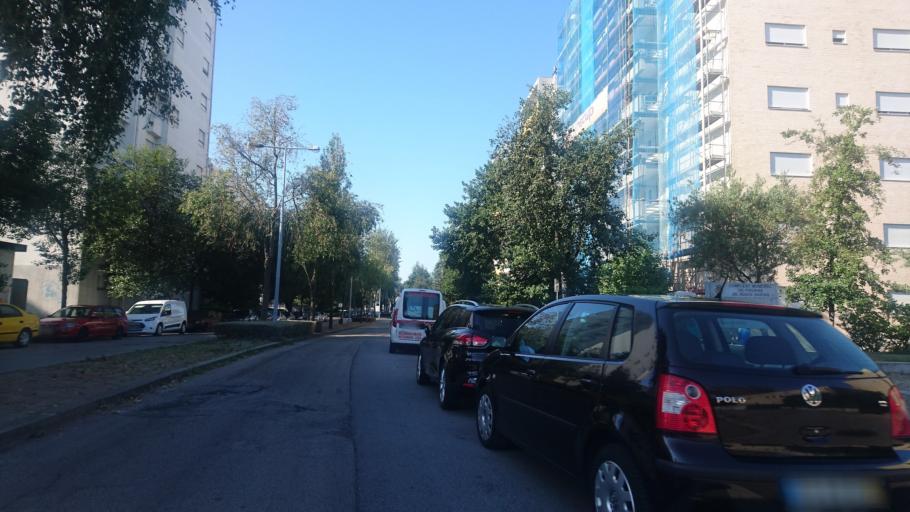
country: PT
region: Porto
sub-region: Valongo
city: Ermesinde
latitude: 41.2044
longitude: -8.5643
